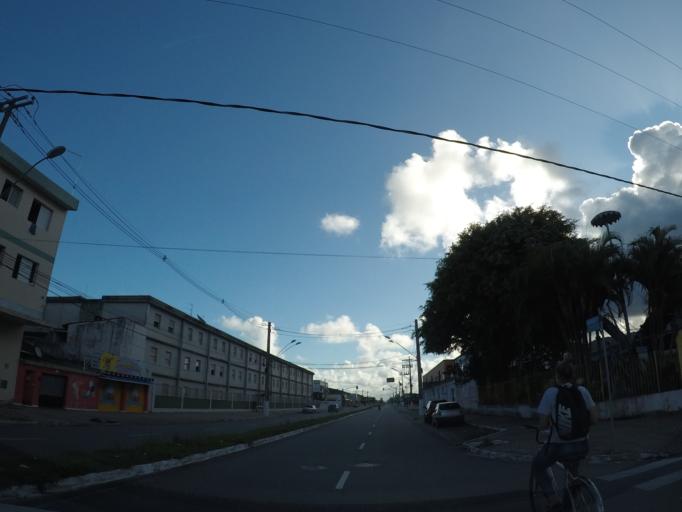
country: BR
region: Sao Paulo
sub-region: Mongagua
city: Mongagua
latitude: -24.0618
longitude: -46.5603
